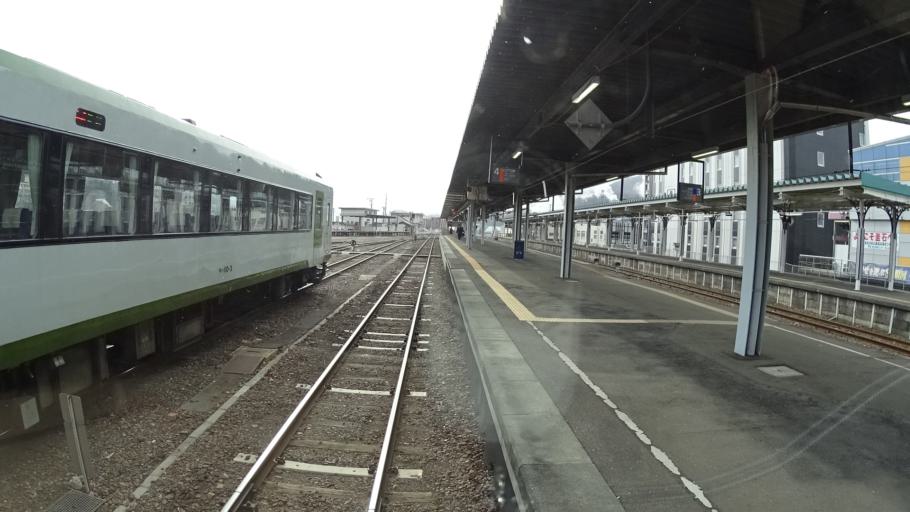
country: JP
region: Iwate
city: Kamaishi
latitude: 39.2737
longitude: 141.8723
